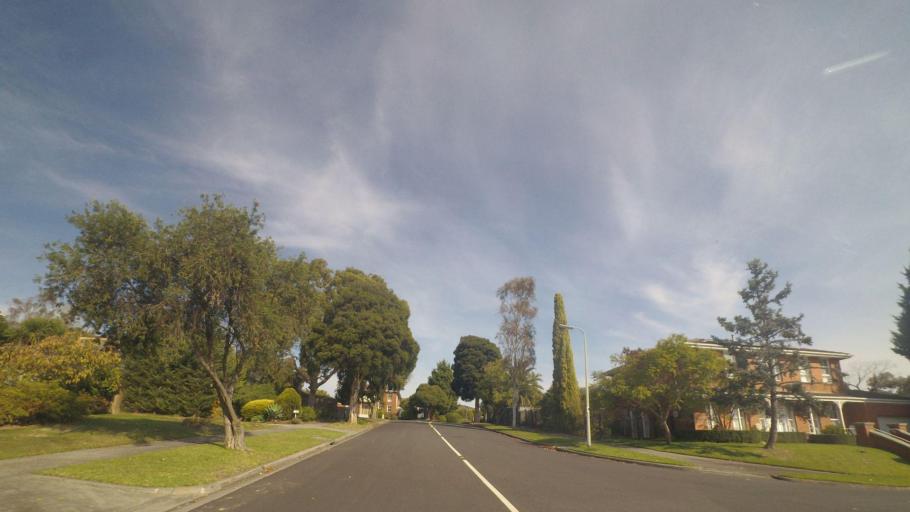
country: AU
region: Victoria
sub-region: Manningham
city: Doncaster East
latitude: -37.7716
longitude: 145.1493
